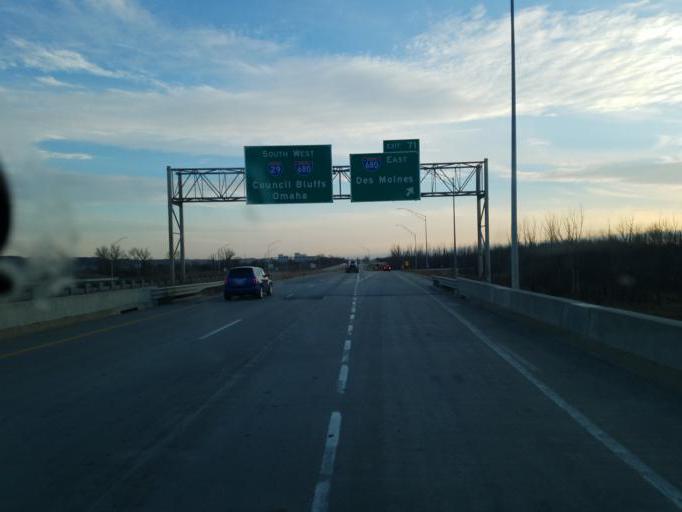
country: US
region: Iowa
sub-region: Harrison County
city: Missouri Valley
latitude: 41.4939
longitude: -95.9013
